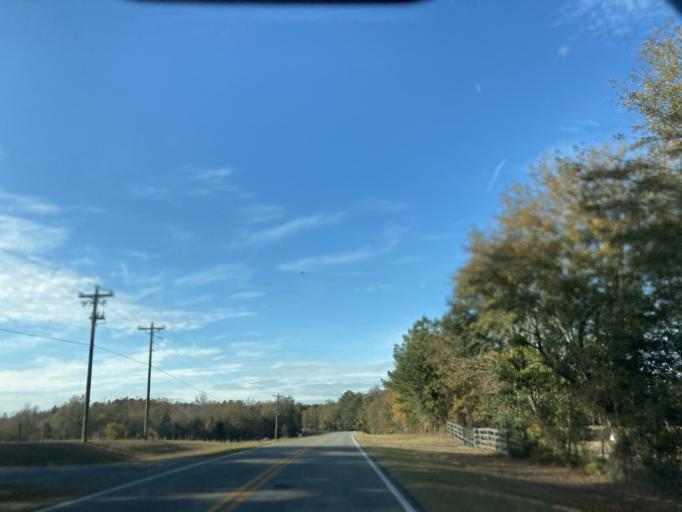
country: US
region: Georgia
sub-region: Jones County
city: Gray
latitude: 32.8943
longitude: -83.5109
